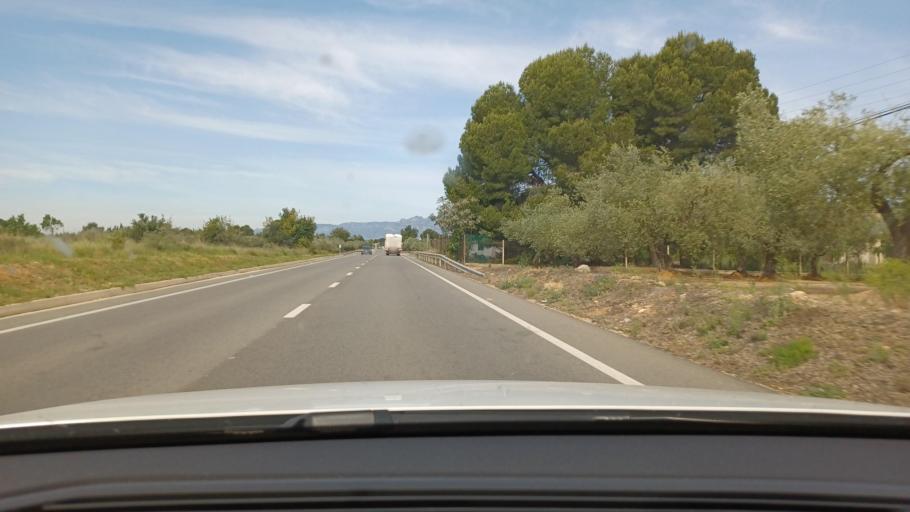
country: ES
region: Catalonia
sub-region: Provincia de Tarragona
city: Masdenverge
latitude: 40.7173
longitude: 0.5153
